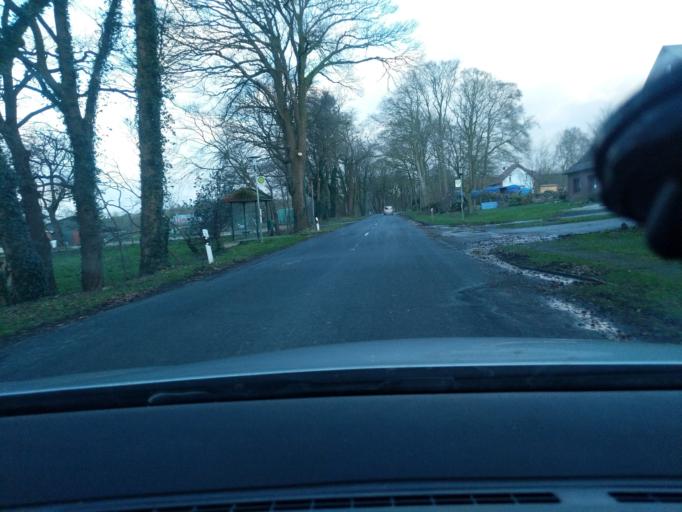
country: DE
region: Lower Saxony
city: Drangstedt
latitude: 53.6416
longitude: 8.7797
